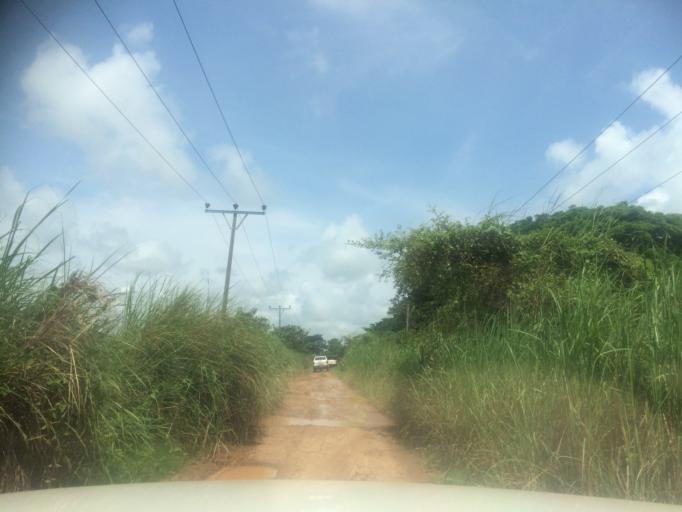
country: MM
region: Bago
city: Tharyarwady
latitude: 17.3161
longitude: 95.8868
